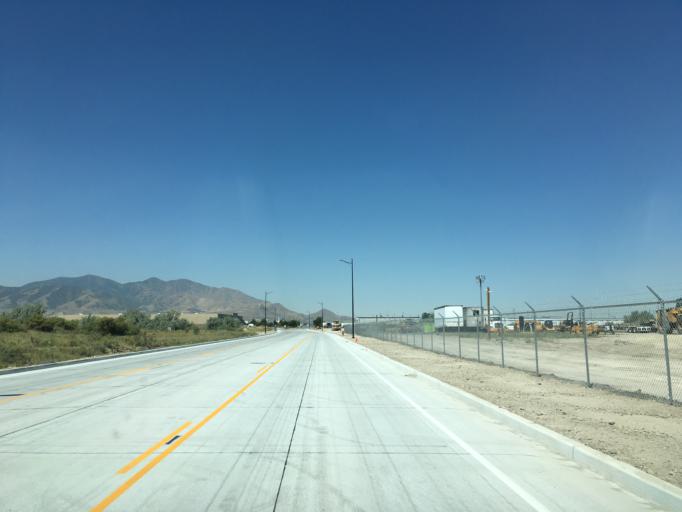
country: US
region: Utah
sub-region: Salt Lake County
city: West Valley City
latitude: 40.7185
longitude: -112.0089
